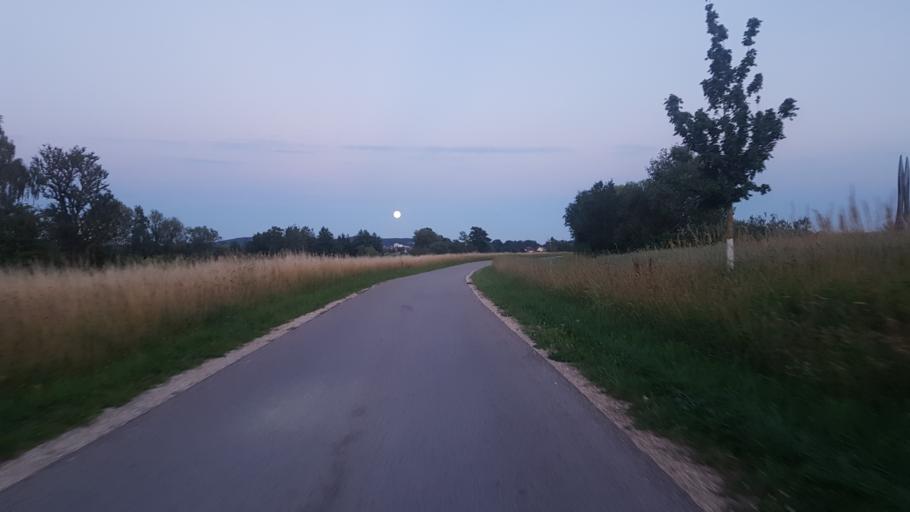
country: DE
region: Bavaria
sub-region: Regierungsbezirk Mittelfranken
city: Muhr am See
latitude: 49.1411
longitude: 10.7315
